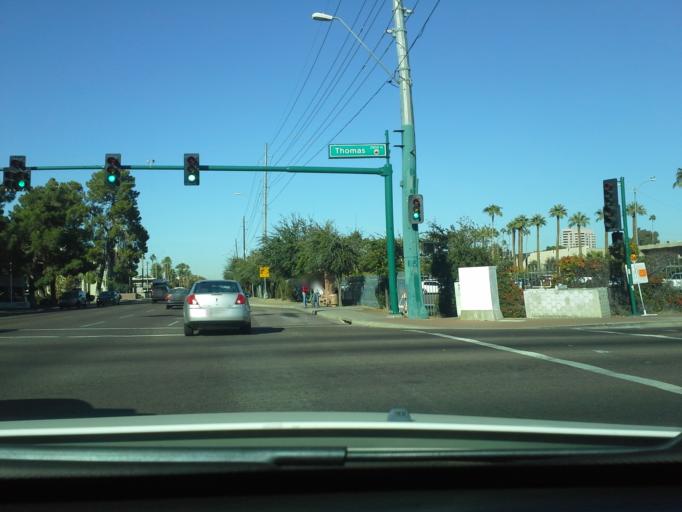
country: US
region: Arizona
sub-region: Maricopa County
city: Phoenix
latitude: 33.4801
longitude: -112.0650
